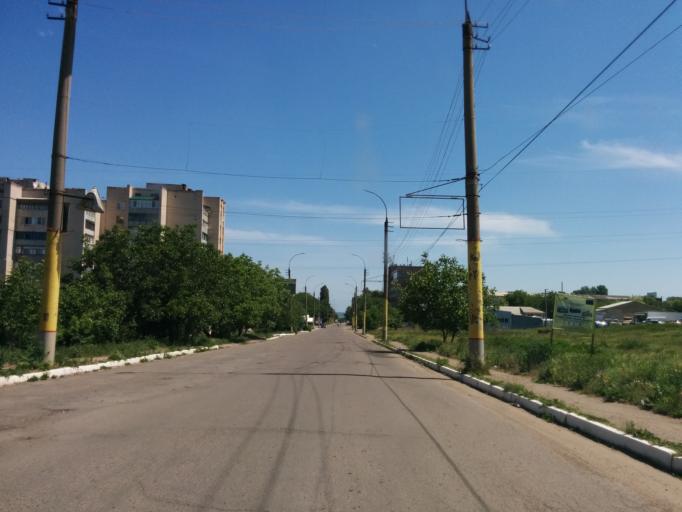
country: MD
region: Raionul Soroca
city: Soroca
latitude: 48.1628
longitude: 28.2659
